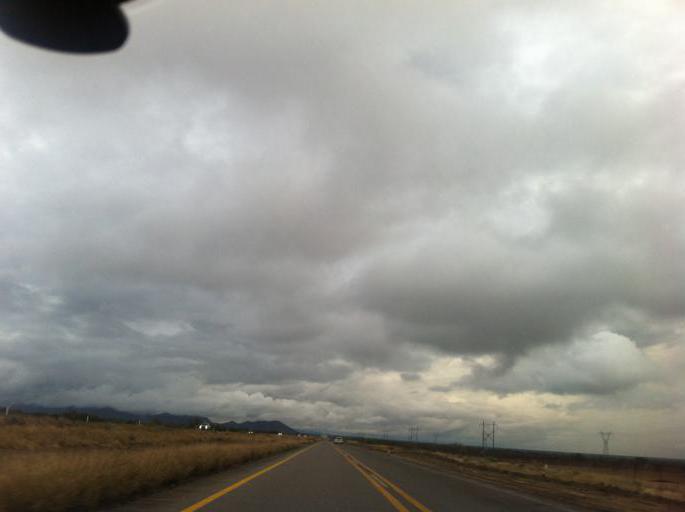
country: MX
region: Sonora
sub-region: San Miguel de Horcasitas
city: Las Mercedes [Agropecuaria]
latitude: 29.5045
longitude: -111.0027
